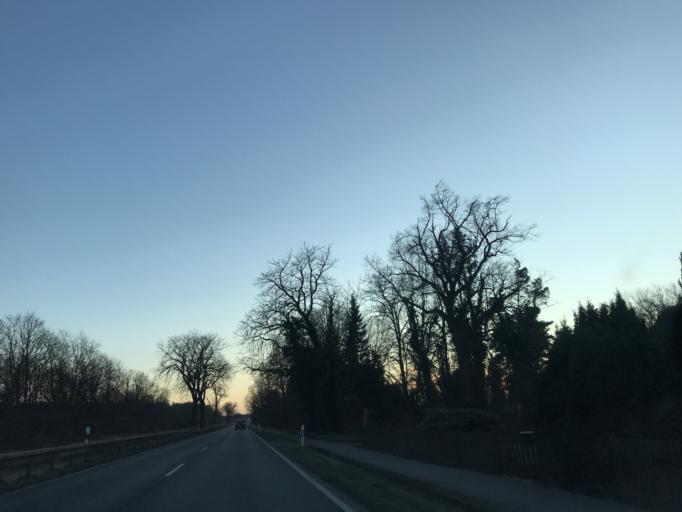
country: DE
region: Brandenburg
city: Rathenow
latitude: 52.5698
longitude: 12.3329
